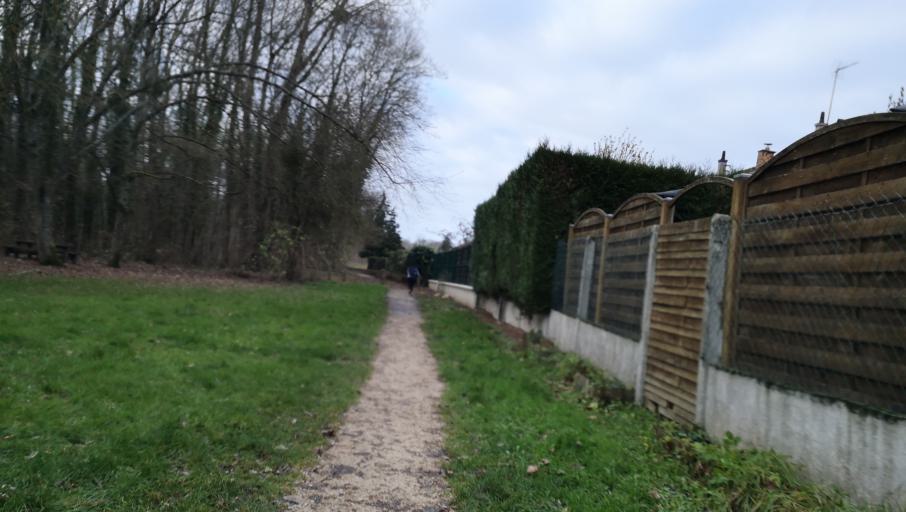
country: FR
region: Centre
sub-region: Departement du Loiret
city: Saint-Jean-de-Braye
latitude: 47.9155
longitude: 1.9992
